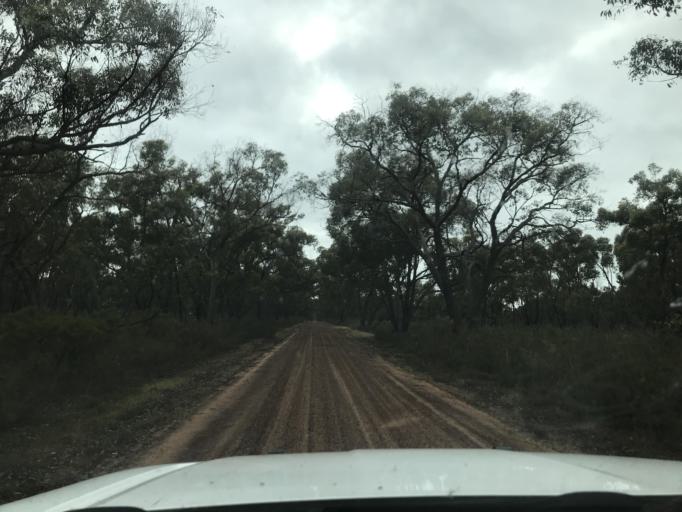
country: AU
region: South Australia
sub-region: Wattle Range
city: Penola
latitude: -37.1181
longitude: 141.1293
